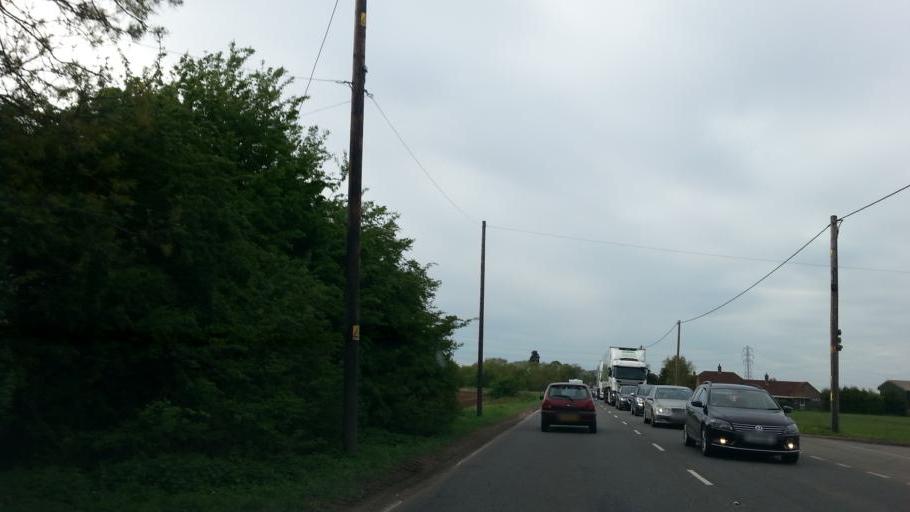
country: GB
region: England
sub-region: Cambridgeshire
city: March
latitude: 52.5712
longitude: 0.0588
